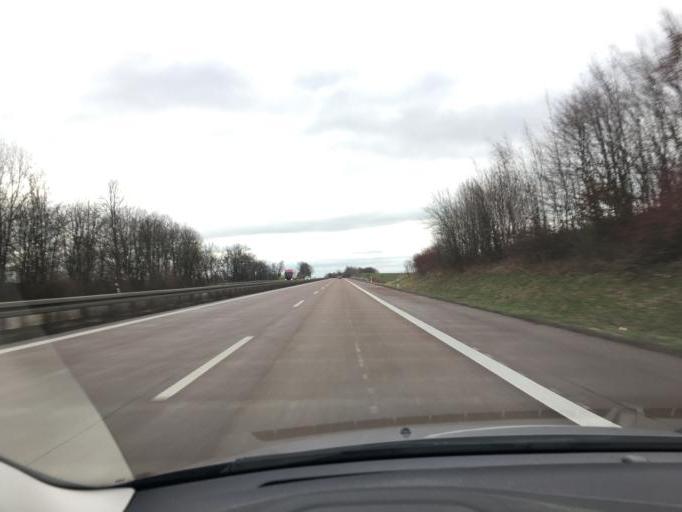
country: DE
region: Saxony
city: Ostrau
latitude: 51.2306
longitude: 12.8942
